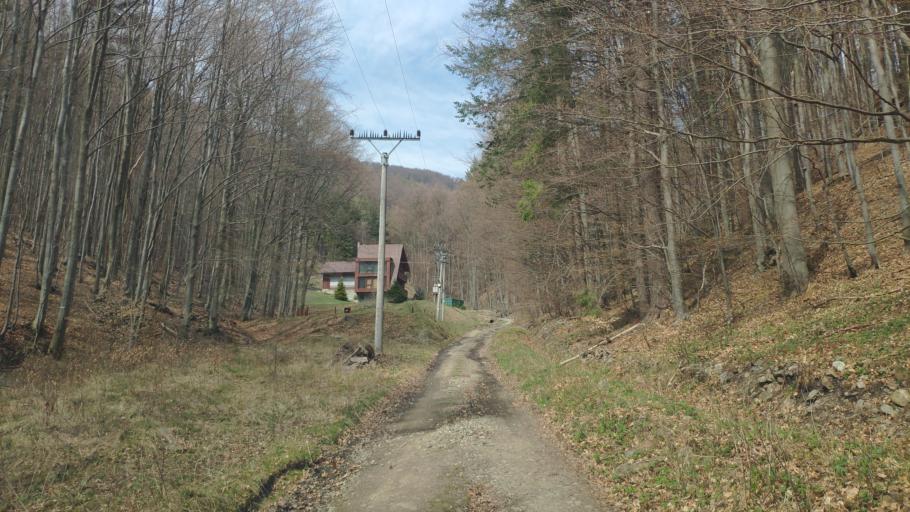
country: SK
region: Kosicky
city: Gelnica
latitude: 48.7532
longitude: 21.0269
